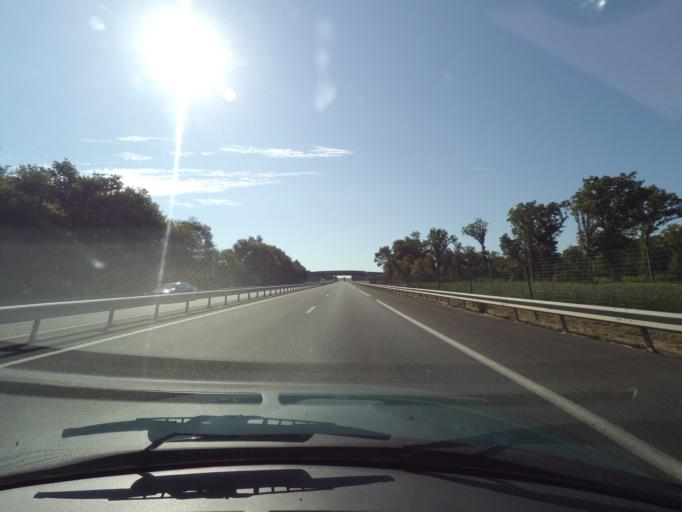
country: FR
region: Poitou-Charentes
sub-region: Departement de la Vienne
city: Savigny-Levescault
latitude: 46.4969
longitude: 0.4896
